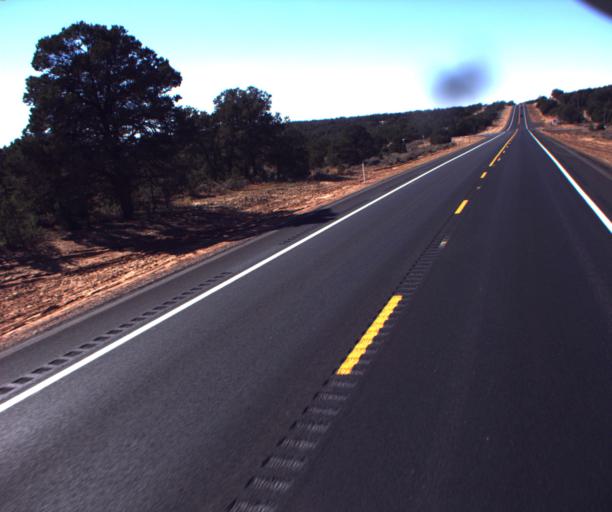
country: US
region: Arizona
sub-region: Apache County
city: Ganado
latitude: 35.7163
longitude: -109.3456
